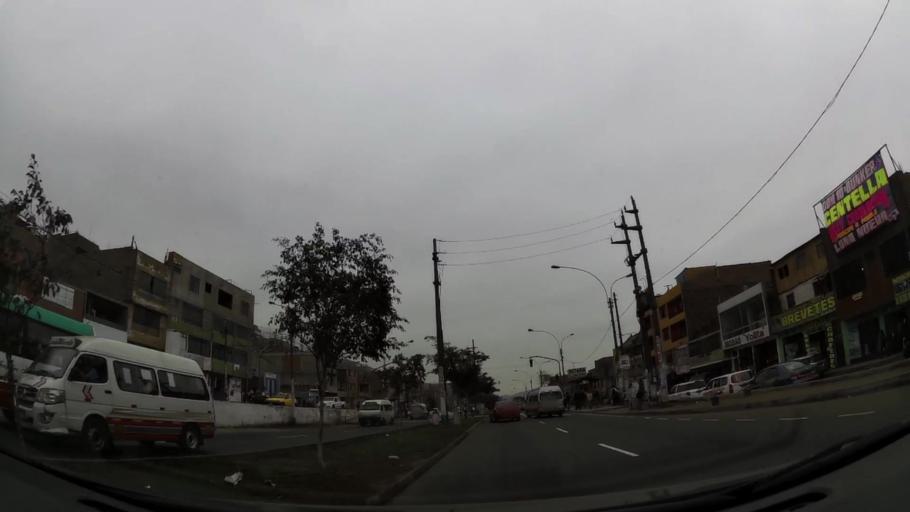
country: PE
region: Lima
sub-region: Lima
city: Independencia
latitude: -11.9595
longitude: -77.0537
